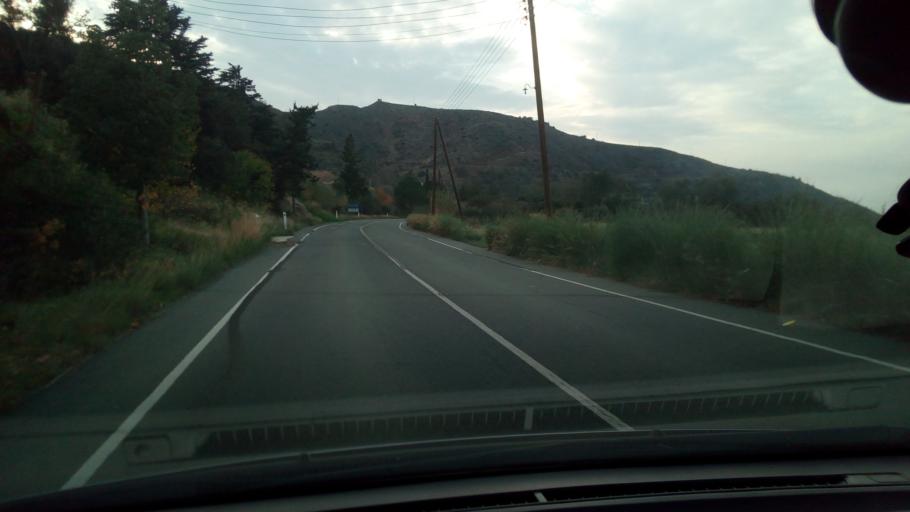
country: CY
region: Lefkosia
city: Kato Pyrgos
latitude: 35.1686
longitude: 32.5665
